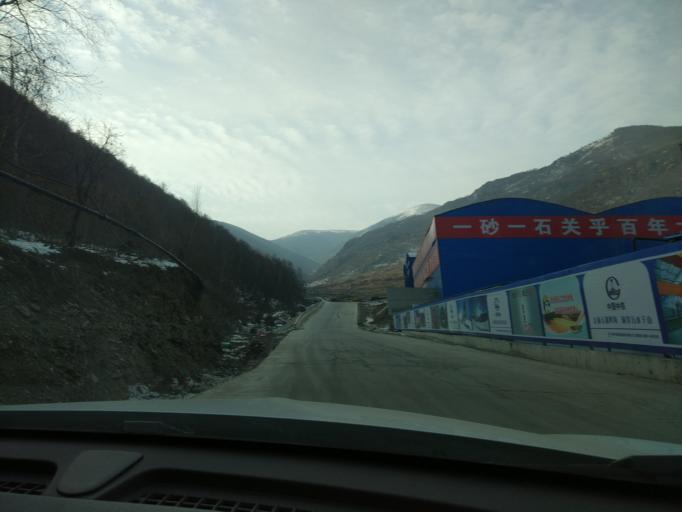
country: CN
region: Hebei
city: Xiwanzi
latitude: 40.8496
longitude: 115.4690
